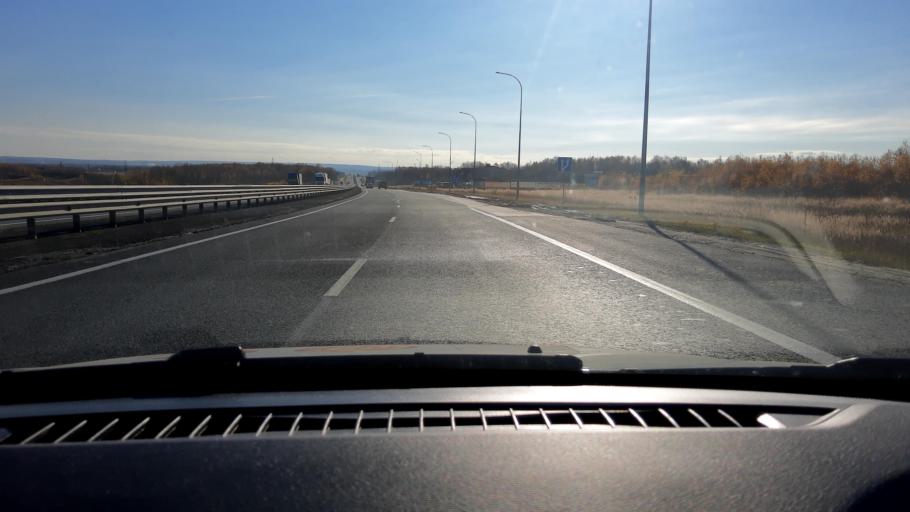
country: RU
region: Nizjnij Novgorod
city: Burevestnik
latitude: 56.1455
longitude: 43.7534
